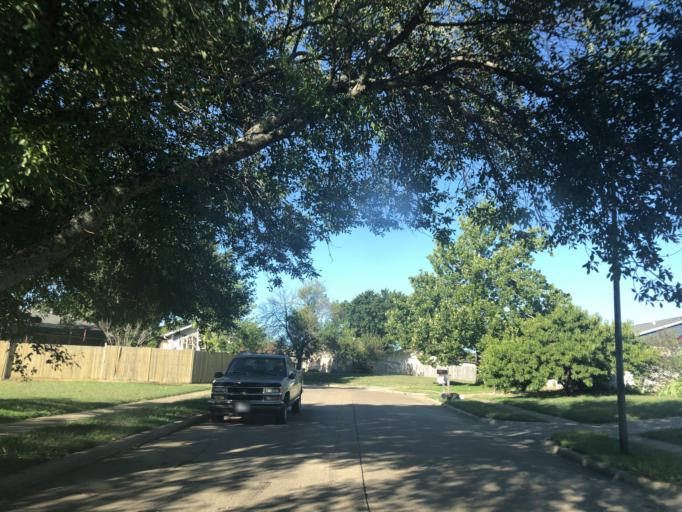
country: US
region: Texas
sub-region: Dallas County
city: Cedar Hill
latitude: 32.6343
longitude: -96.9526
